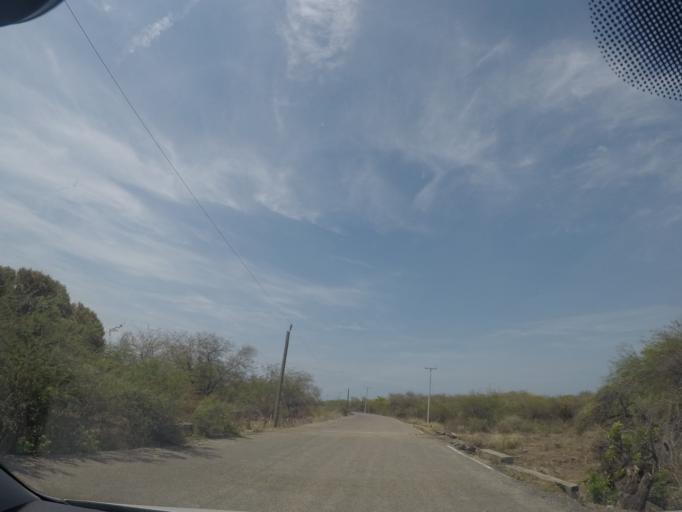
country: MX
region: Oaxaca
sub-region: Salina Cruz
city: Salina Cruz
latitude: 16.2085
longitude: -95.1216
